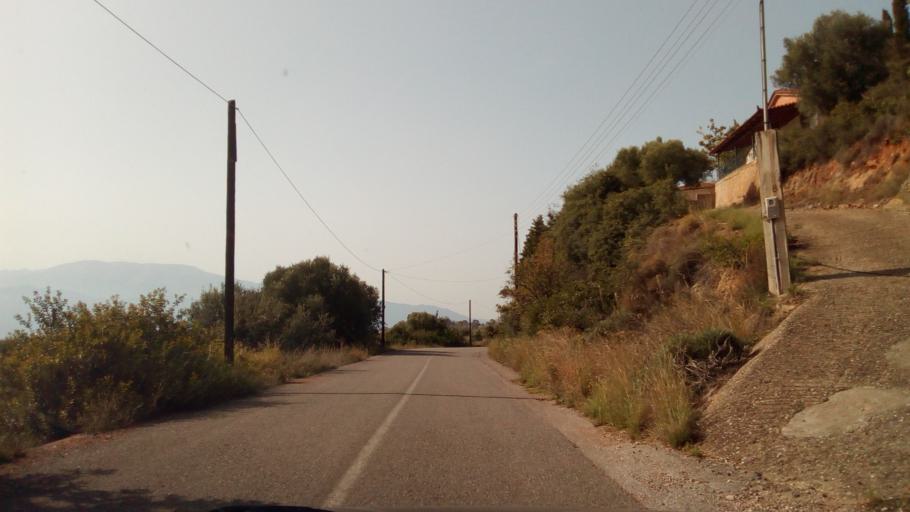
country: GR
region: West Greece
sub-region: Nomos Aitolias kai Akarnanias
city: Nafpaktos
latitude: 38.4035
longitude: 21.9293
